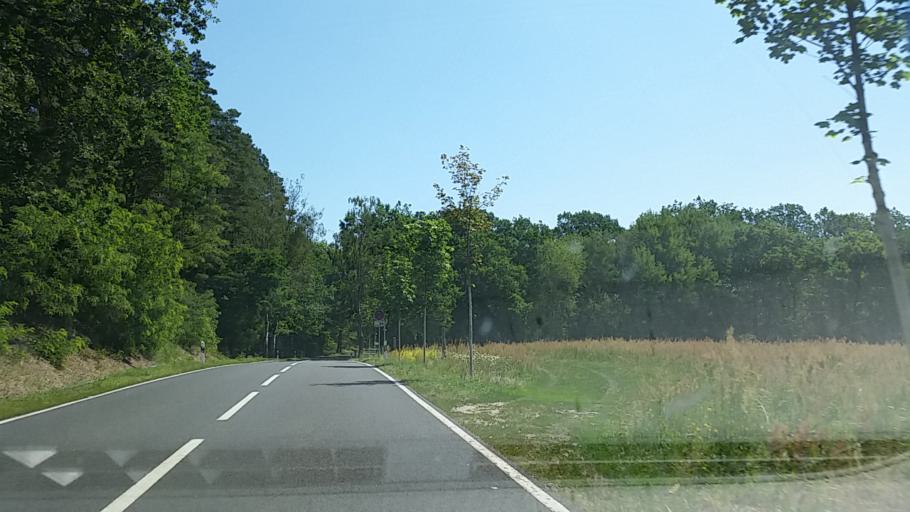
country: DE
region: Saxony-Anhalt
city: Pretzsch
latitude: 51.6883
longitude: 12.7872
